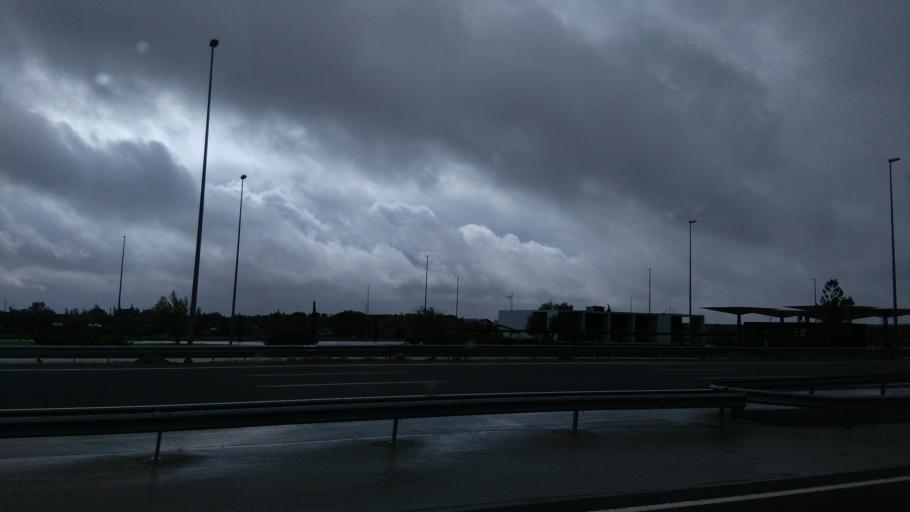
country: ES
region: Madrid
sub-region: Provincia de Madrid
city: Alcorcon
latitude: 40.3368
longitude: -3.8032
